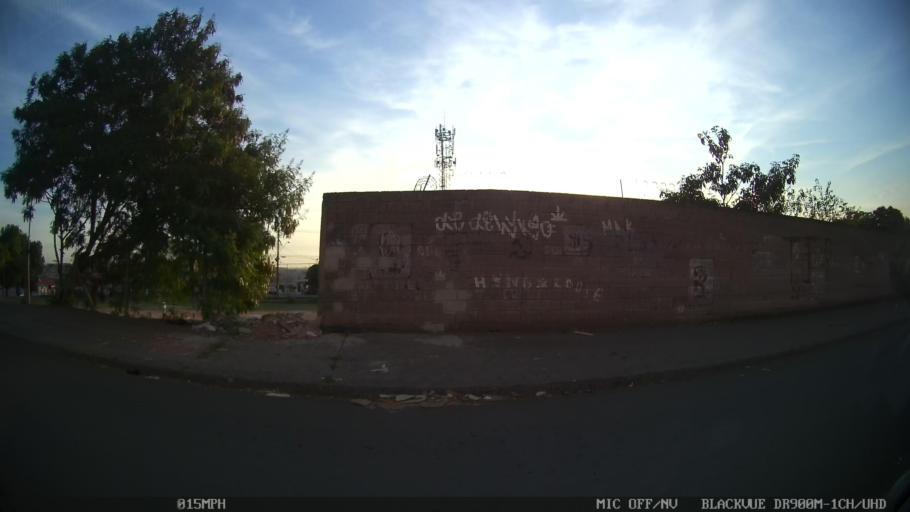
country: BR
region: Sao Paulo
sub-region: Campinas
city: Campinas
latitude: -22.9796
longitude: -47.1323
